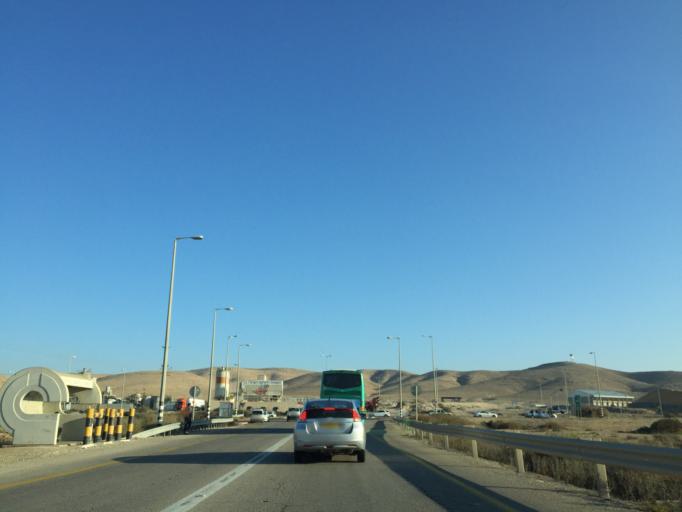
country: IL
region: Southern District
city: Dimona
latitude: 31.0670
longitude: 35.0059
